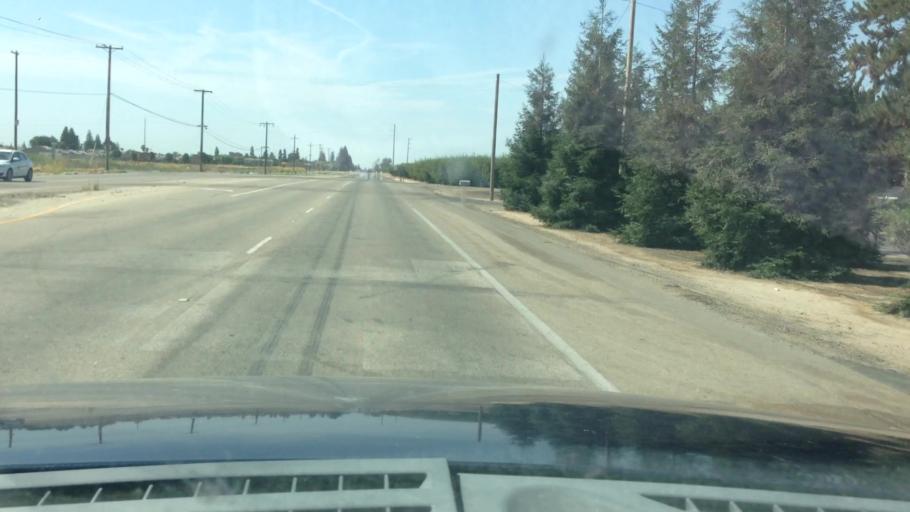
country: US
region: California
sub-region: Fresno County
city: Parlier
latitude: 36.6207
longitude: -119.5569
